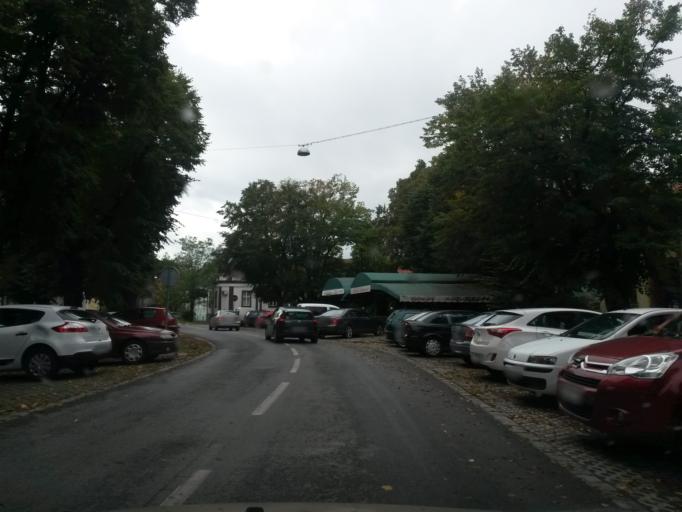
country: HR
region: Osjecko-Baranjska
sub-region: Grad Osijek
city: Osijek
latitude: 45.5553
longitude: 18.6885
